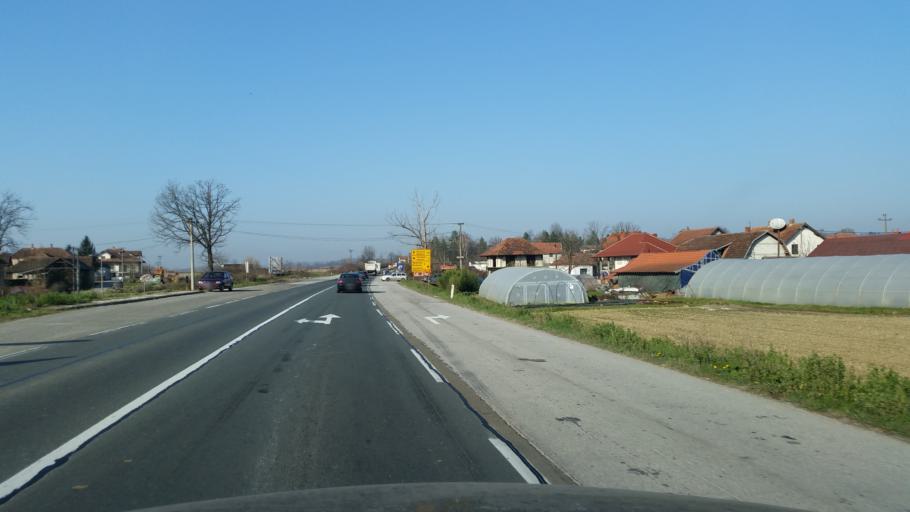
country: RS
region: Central Serbia
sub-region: Kolubarski Okrug
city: Ljig
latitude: 44.2943
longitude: 20.2630
